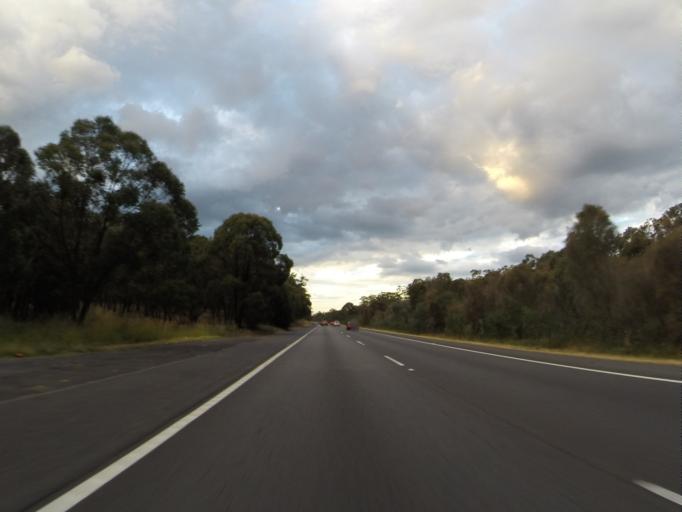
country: AU
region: New South Wales
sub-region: Wollondilly
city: Douglas Park
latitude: -34.2040
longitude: 150.6994
